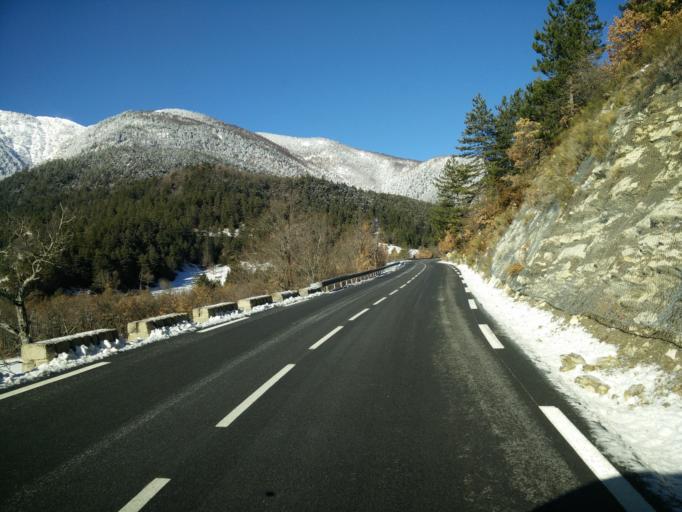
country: FR
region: Provence-Alpes-Cote d'Azur
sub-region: Departement des Alpes-de-Haute-Provence
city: Annot
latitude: 43.9324
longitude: 6.6398
